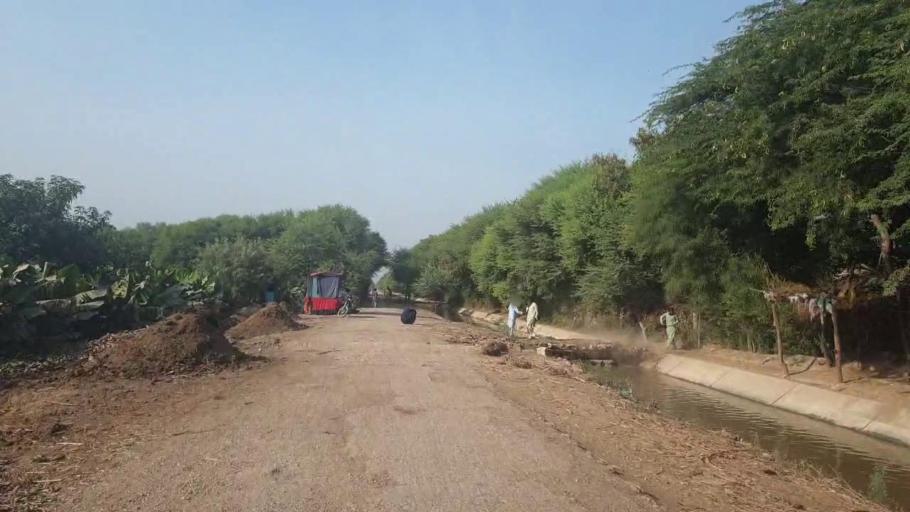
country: PK
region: Sindh
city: Tando Jam
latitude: 25.4198
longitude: 68.4629
